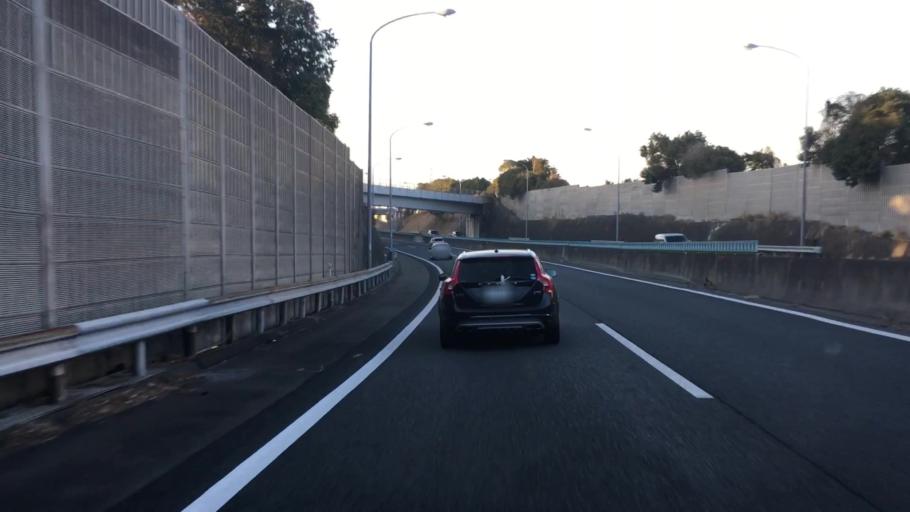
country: JP
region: Kanagawa
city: Kamakura
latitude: 35.3709
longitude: 139.5935
